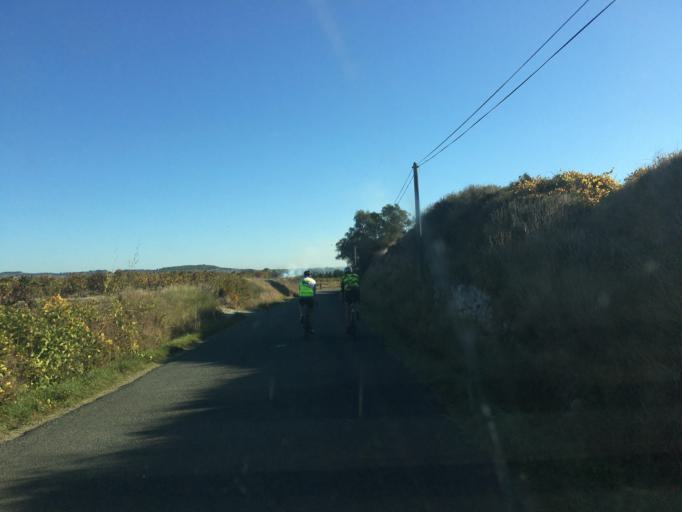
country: FR
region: Languedoc-Roussillon
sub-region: Departement de l'Aude
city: Fleury
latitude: 43.2339
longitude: 3.1485
